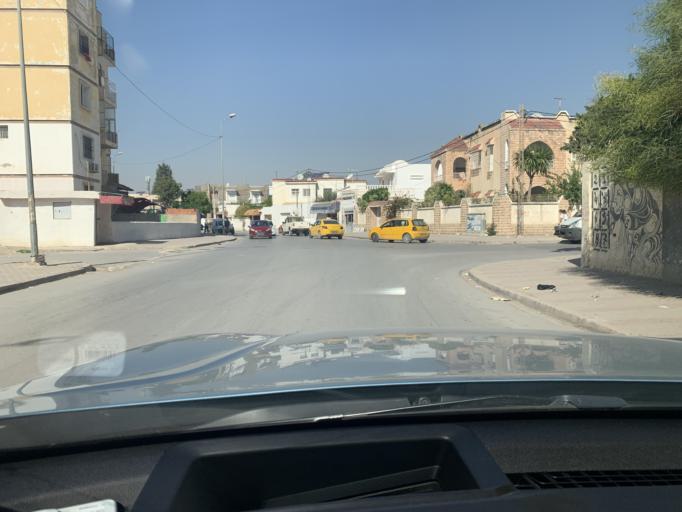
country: TN
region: Manouba
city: Manouba
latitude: 36.8254
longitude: 10.1184
